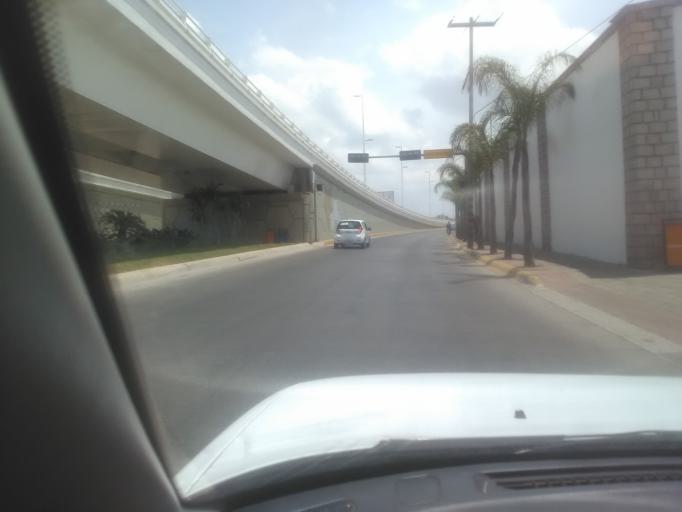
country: MX
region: Durango
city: Victoria de Durango
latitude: 24.0355
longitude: -104.6823
